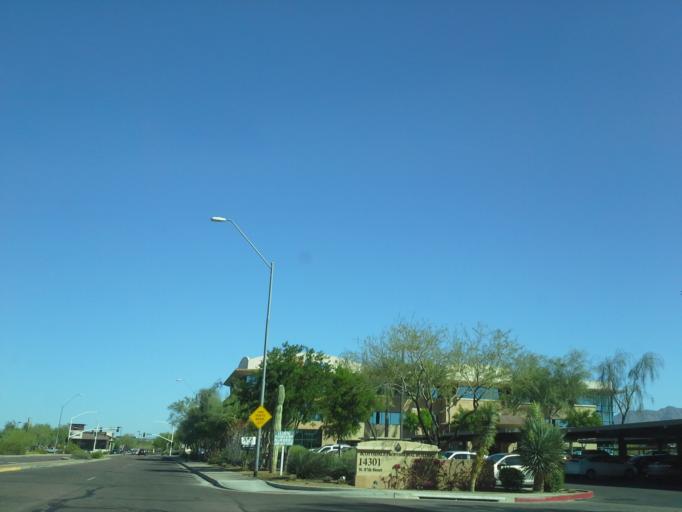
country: US
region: Arizona
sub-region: Maricopa County
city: Paradise Valley
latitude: 33.6163
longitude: -111.8931
